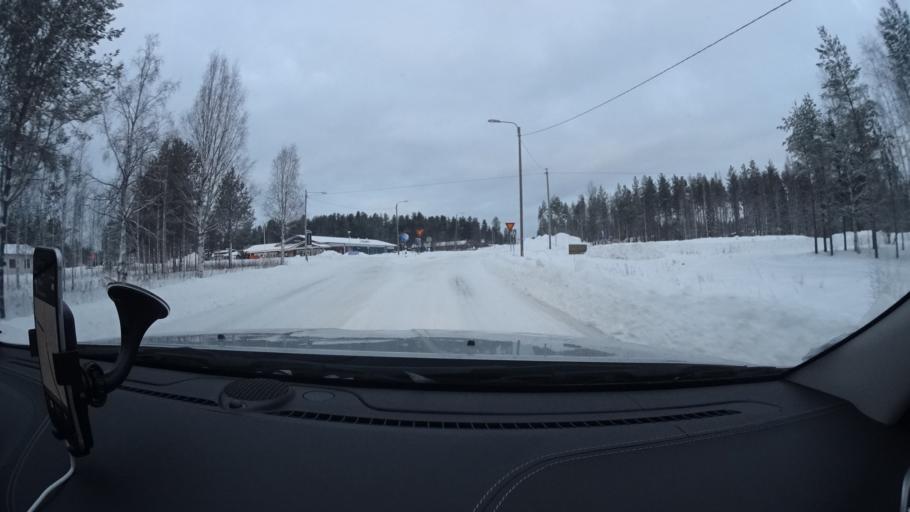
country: FI
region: Lapland
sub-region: Rovaniemi
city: Ranua
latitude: 66.3761
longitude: 26.6822
